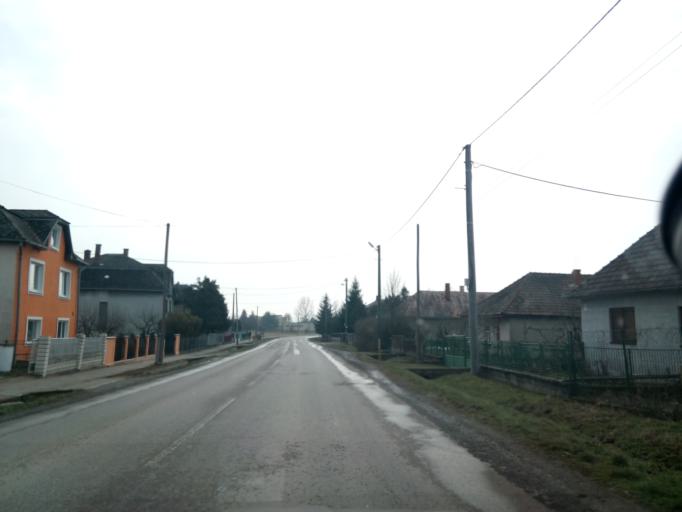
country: SK
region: Kosicky
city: Secovce
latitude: 48.6463
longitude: 21.5762
